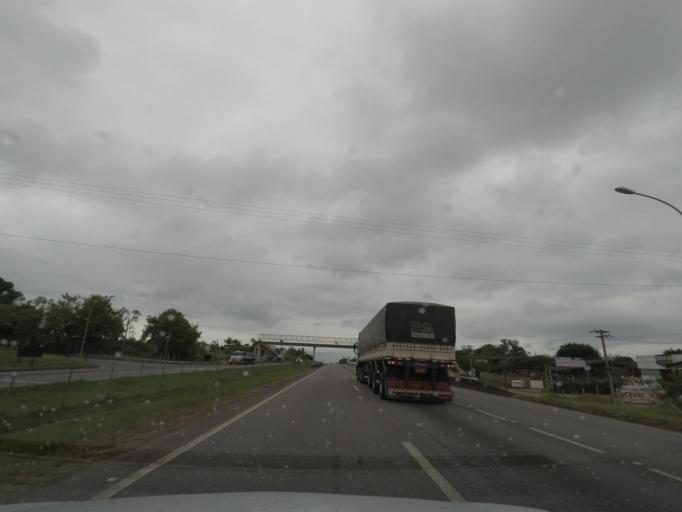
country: BR
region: Sao Paulo
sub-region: Registro
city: Registro
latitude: -24.4592
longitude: -47.8157
